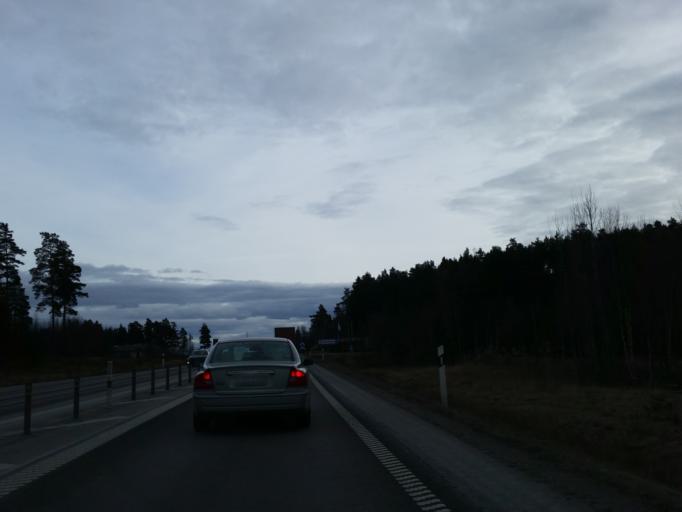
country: SE
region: OEstergoetland
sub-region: Soderkopings Kommun
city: Soederkoeping
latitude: 58.4995
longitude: 16.3018
